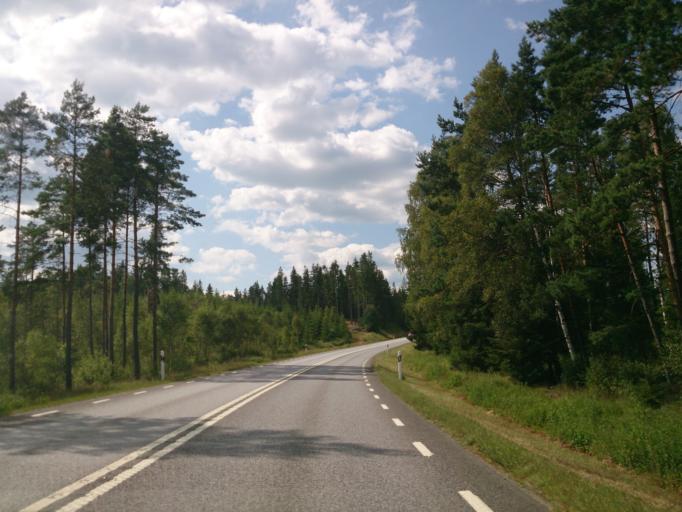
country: SE
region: Joenkoeping
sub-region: Gislaveds Kommun
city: Smalandsstenar
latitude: 57.1565
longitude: 13.4863
